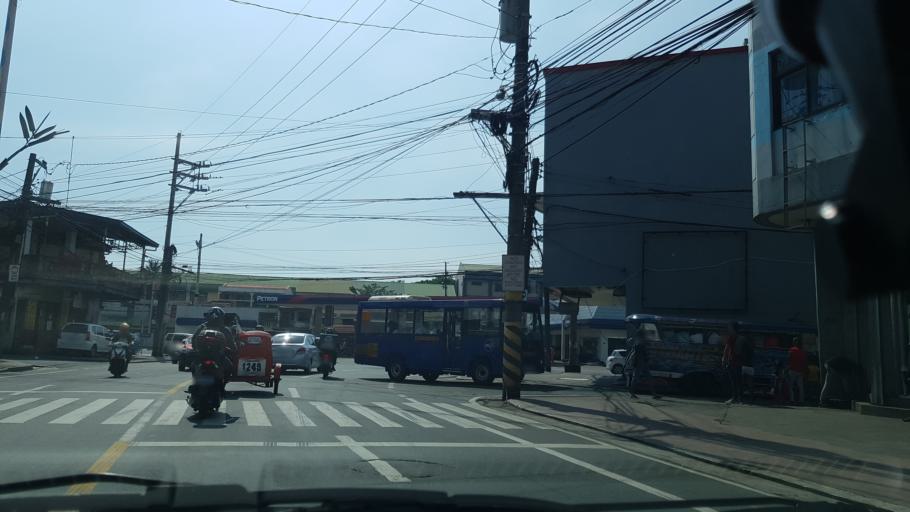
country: PH
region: Metro Manila
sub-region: Marikina
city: Calumpang
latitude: 14.6508
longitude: 121.1034
